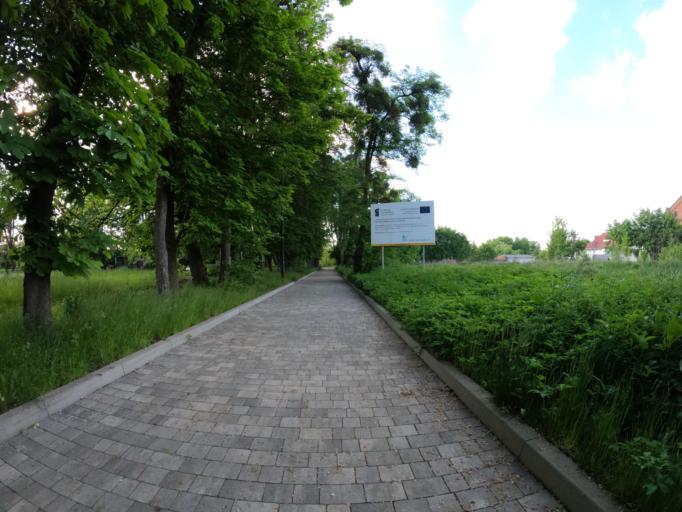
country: PL
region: Warmian-Masurian Voivodeship
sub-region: Powiat lidzbarski
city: Lidzbark Warminski
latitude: 54.1267
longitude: 20.5925
